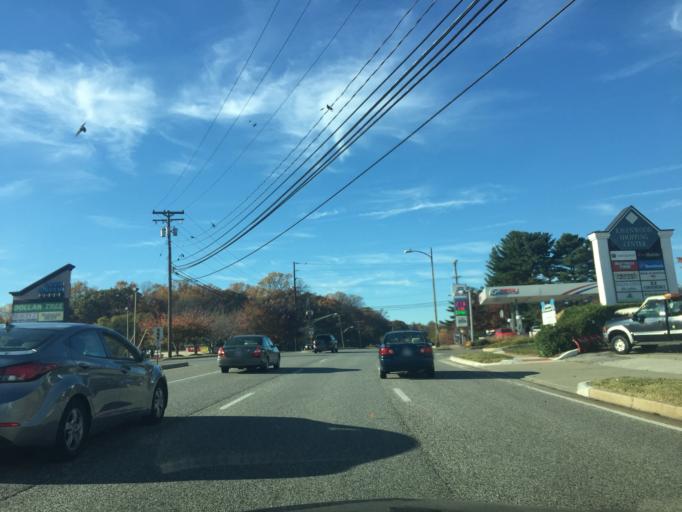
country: US
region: Maryland
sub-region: Baltimore County
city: Towson
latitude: 39.3858
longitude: -76.5779
